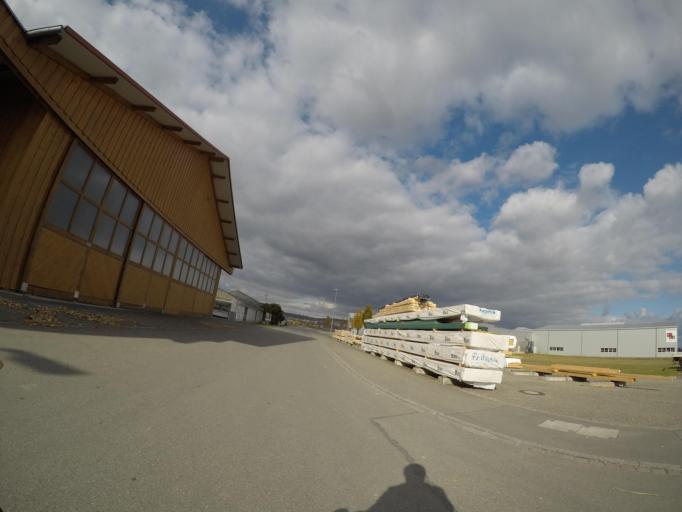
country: DE
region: Baden-Wuerttemberg
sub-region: Tuebingen Region
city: Emerkingen
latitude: 48.2159
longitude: 9.6578
